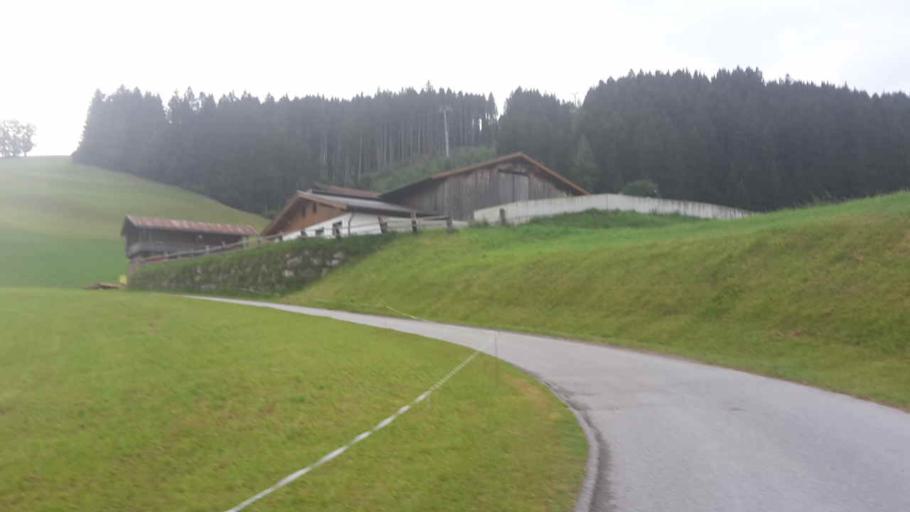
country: AT
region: Tyrol
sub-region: Politischer Bezirk Kitzbuhel
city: Kirchberg in Tirol
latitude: 47.4381
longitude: 12.3246
